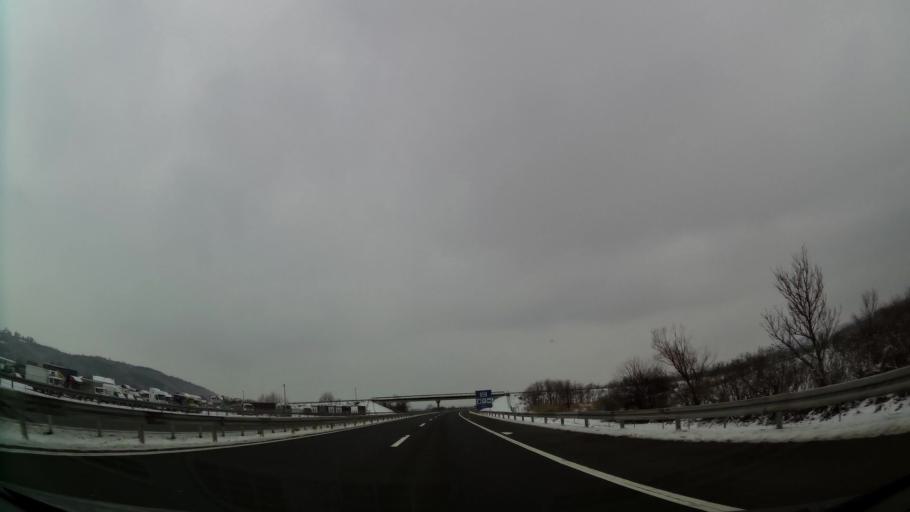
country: RS
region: Central Serbia
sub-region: Sumadijski Okrug
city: Batocina
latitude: 44.1235
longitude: 21.1407
